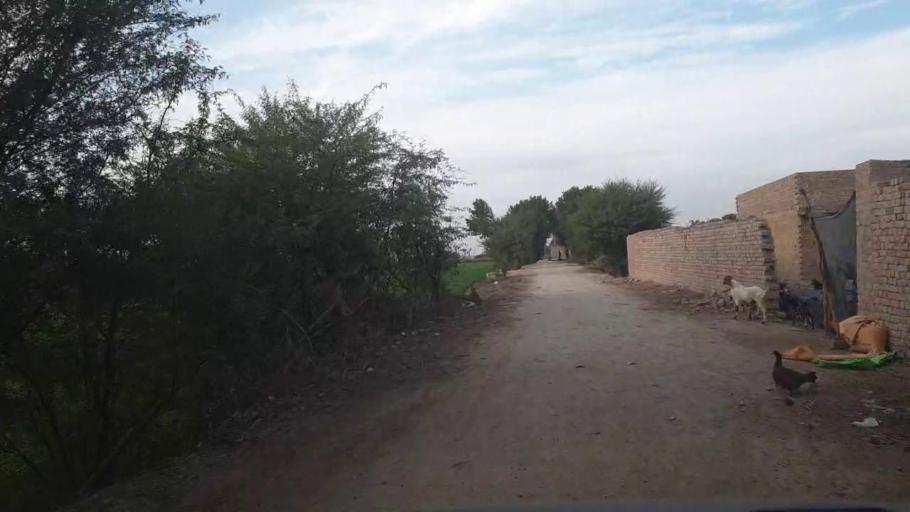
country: PK
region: Sindh
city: Shahpur Chakar
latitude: 26.1440
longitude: 68.6279
